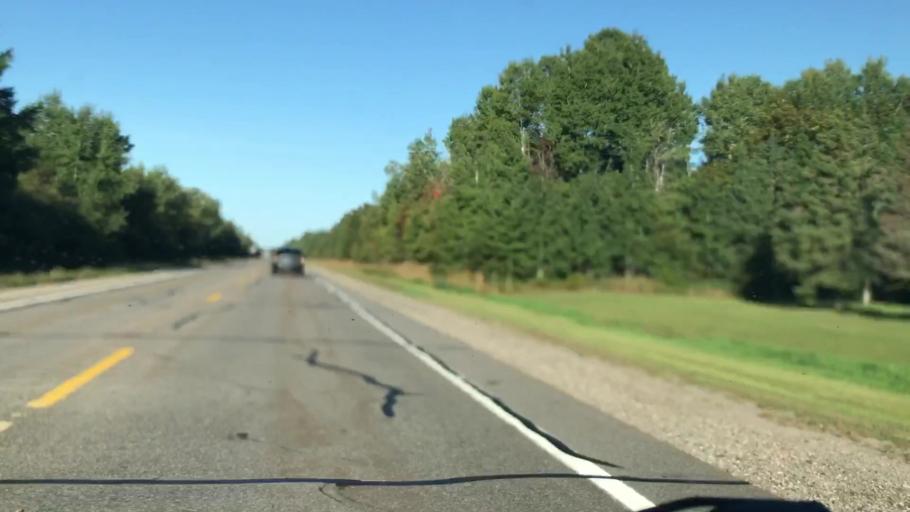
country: US
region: Michigan
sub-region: Chippewa County
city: Sault Ste. Marie
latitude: 46.3758
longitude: -84.6281
